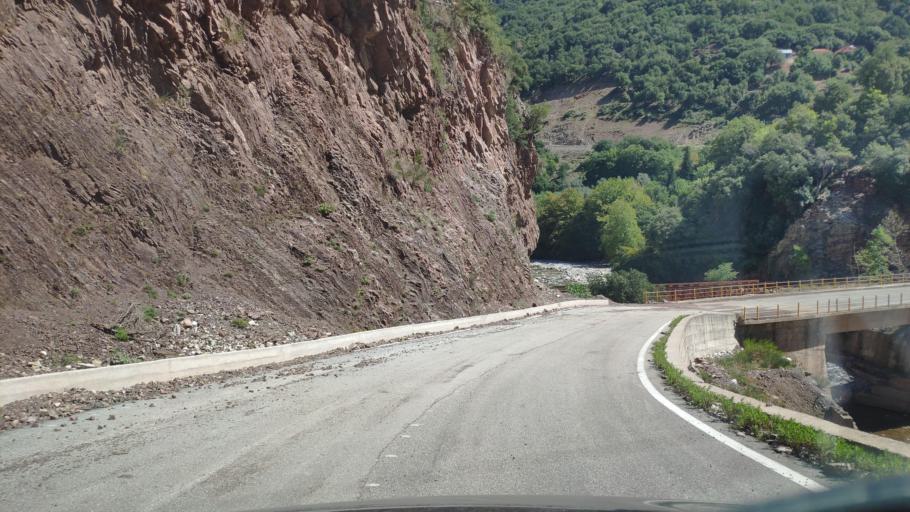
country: GR
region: Central Greece
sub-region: Nomos Evrytanias
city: Kerasochori
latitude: 39.0898
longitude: 21.6016
